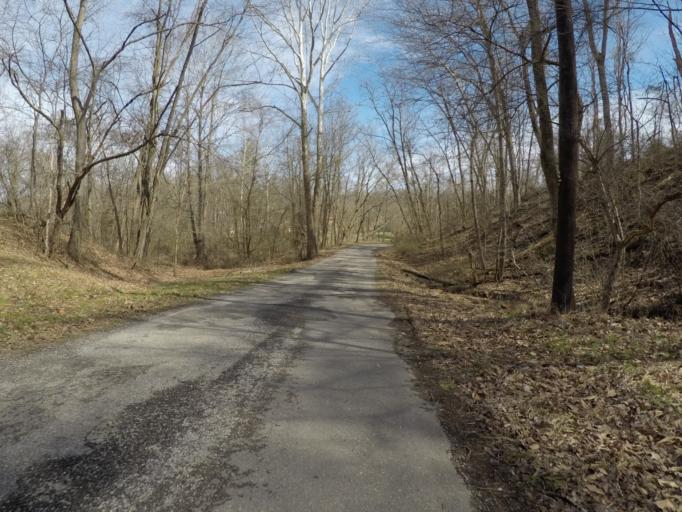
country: US
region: West Virginia
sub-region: Wayne County
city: Ceredo
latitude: 38.3623
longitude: -82.5329
